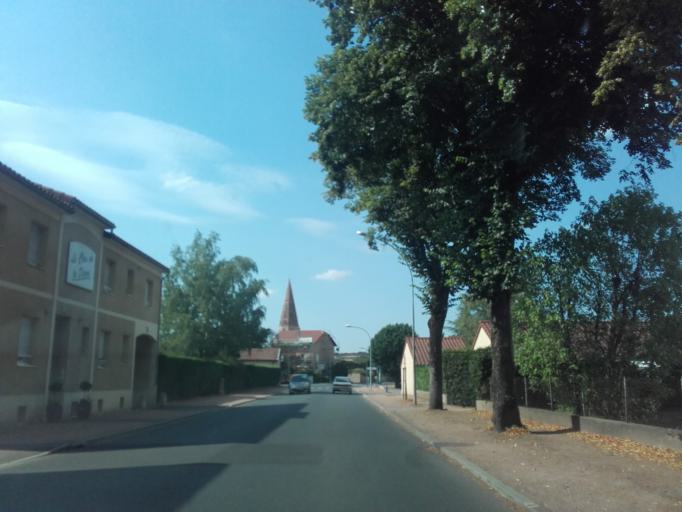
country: FR
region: Bourgogne
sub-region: Departement de Saone-et-Loire
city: Cluny
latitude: 46.4290
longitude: 4.6633
